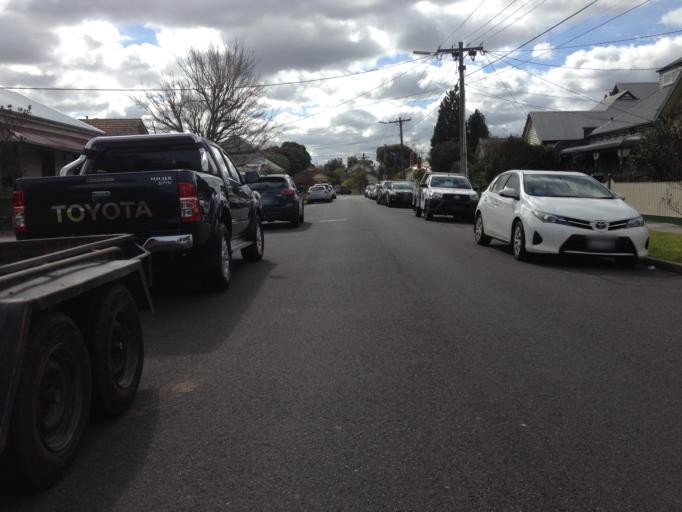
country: AU
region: Victoria
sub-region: Darebin
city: Fairfield
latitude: -37.7817
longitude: 145.0134
